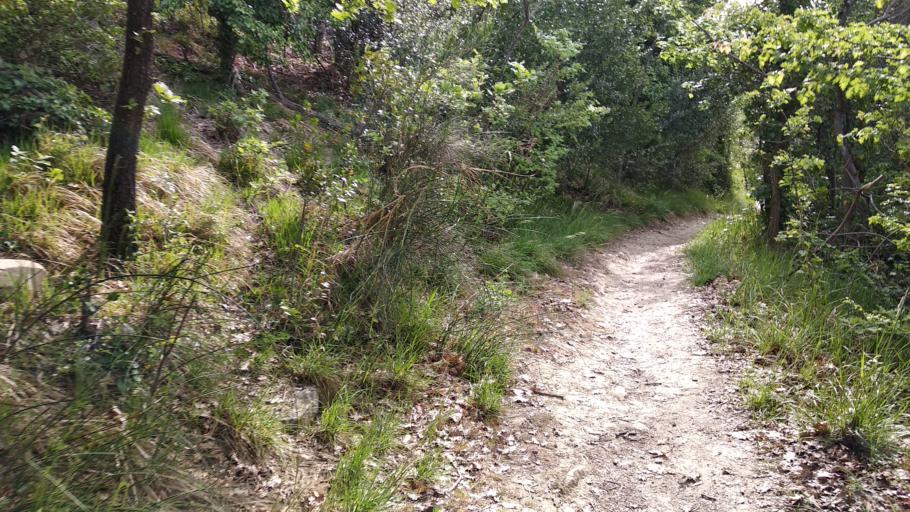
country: IT
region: Emilia-Romagna
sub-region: Provincia di Ravenna
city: Brisighella
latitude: 44.2244
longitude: 11.7582
